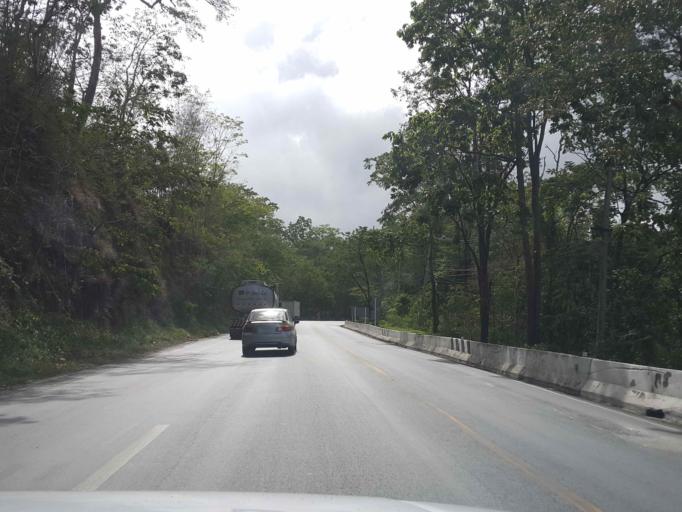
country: TH
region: Tak
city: Tak
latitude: 16.8133
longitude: 98.9737
